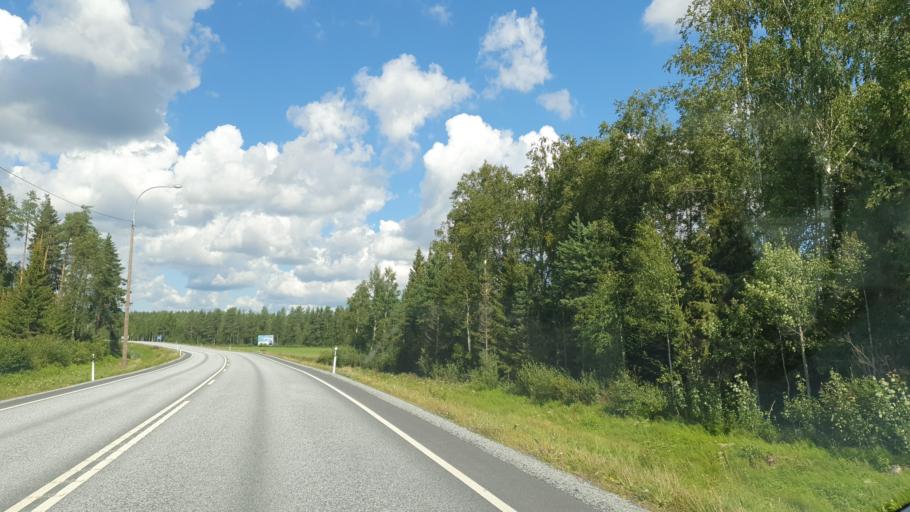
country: FI
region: Northern Savo
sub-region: Ylae-Savo
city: Sonkajaervi
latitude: 63.8816
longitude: 27.4411
